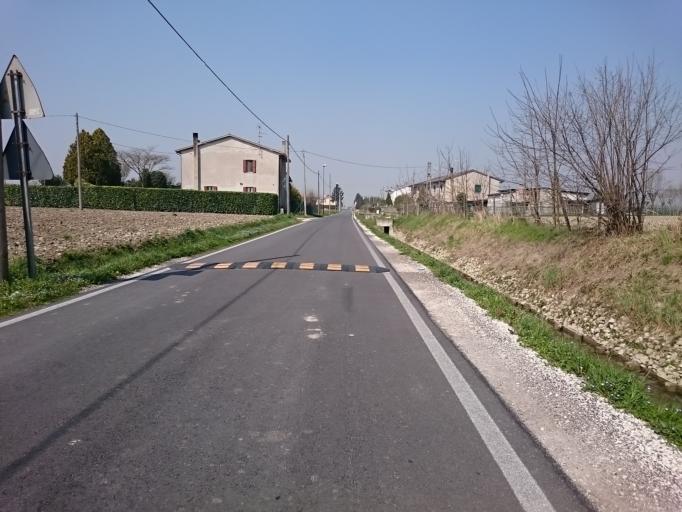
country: IT
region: Veneto
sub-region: Provincia di Padova
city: Villa Estense
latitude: 45.1894
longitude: 11.6750
